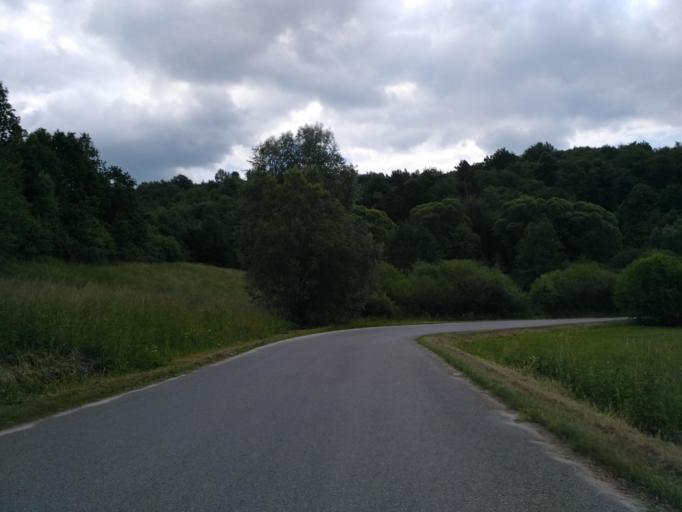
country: PL
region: Subcarpathian Voivodeship
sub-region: Powiat przeworski
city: Jawornik Polski
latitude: 49.8481
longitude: 22.3042
